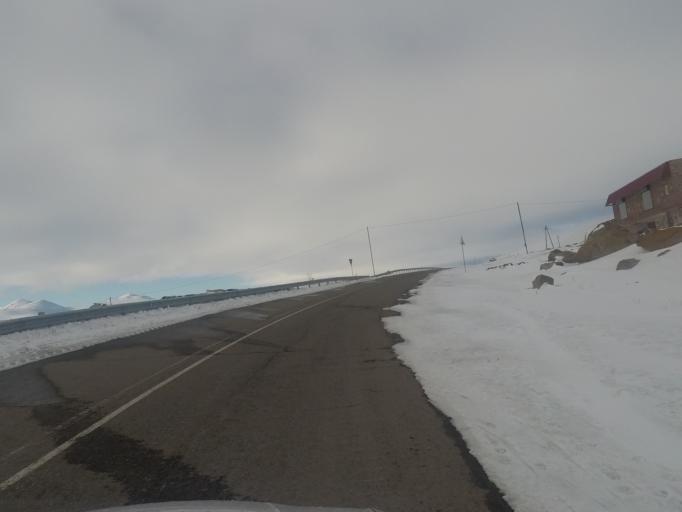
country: GE
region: Kvemo Kartli
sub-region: Tsalka
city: Tsalka
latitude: 41.4527
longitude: 43.8537
